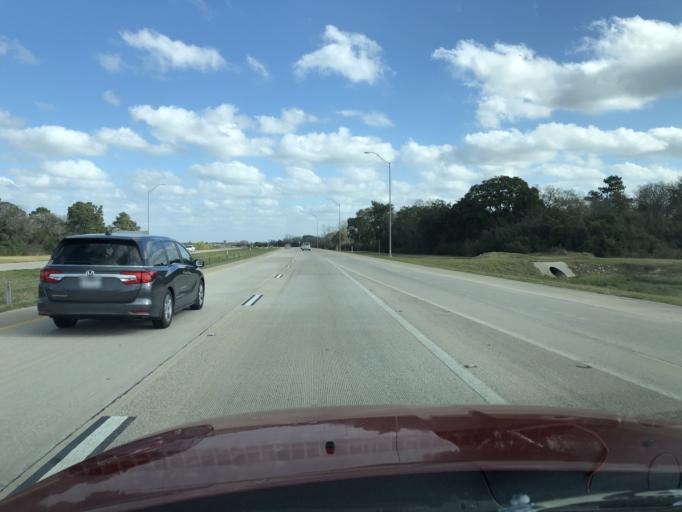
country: US
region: Texas
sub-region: Harris County
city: Cypress
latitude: 30.0510
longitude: -95.6930
